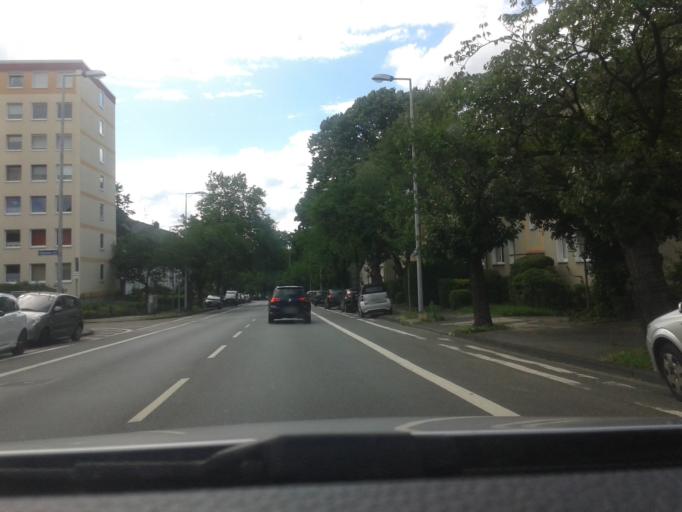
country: DE
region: North Rhine-Westphalia
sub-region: Regierungsbezirk Dusseldorf
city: Muelheim (Ruhr)
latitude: 51.4191
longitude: 6.8518
